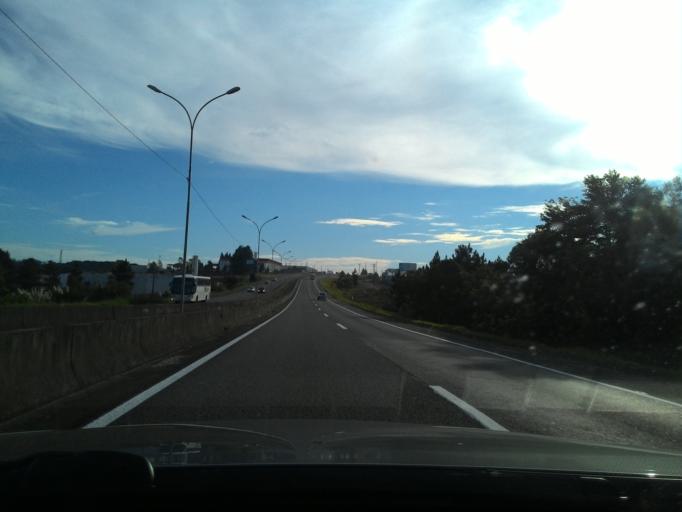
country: BR
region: Parana
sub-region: Quatro Barras
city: Quatro Barras
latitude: -25.3537
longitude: -49.0639
